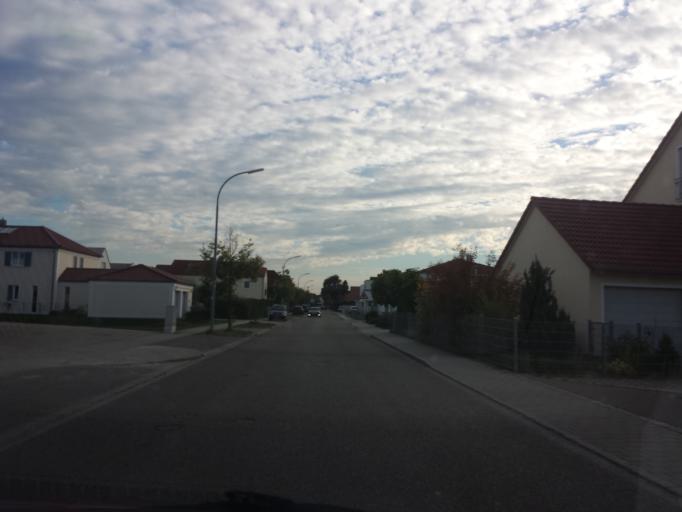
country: DE
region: Bavaria
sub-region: Upper Bavaria
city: Weichering
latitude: 48.7588
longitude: 11.3460
